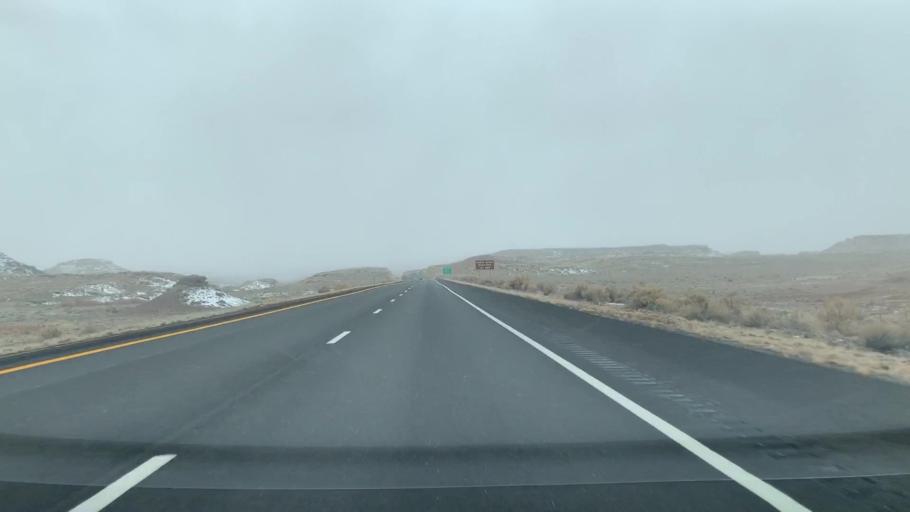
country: US
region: Utah
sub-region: Carbon County
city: East Carbon City
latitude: 38.9313
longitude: -110.3578
